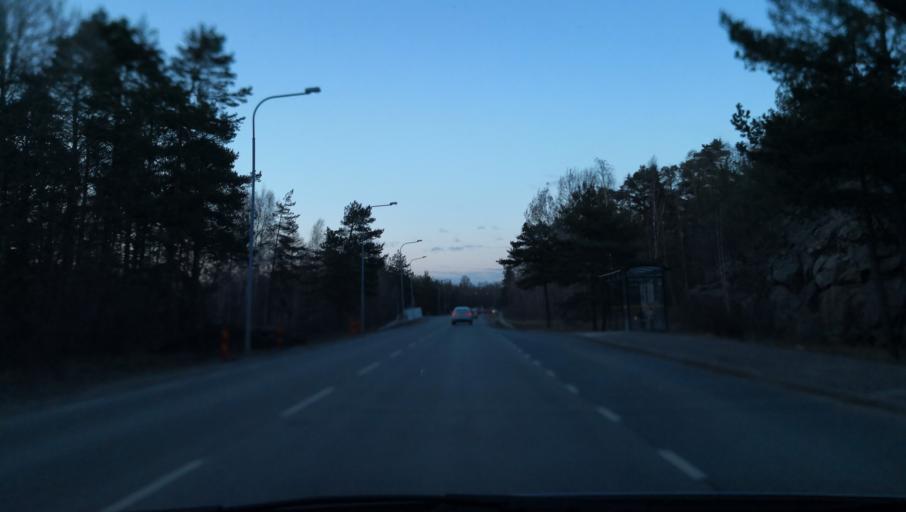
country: SE
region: Stockholm
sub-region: Nacka Kommun
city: Boo
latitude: 59.3279
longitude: 18.2619
